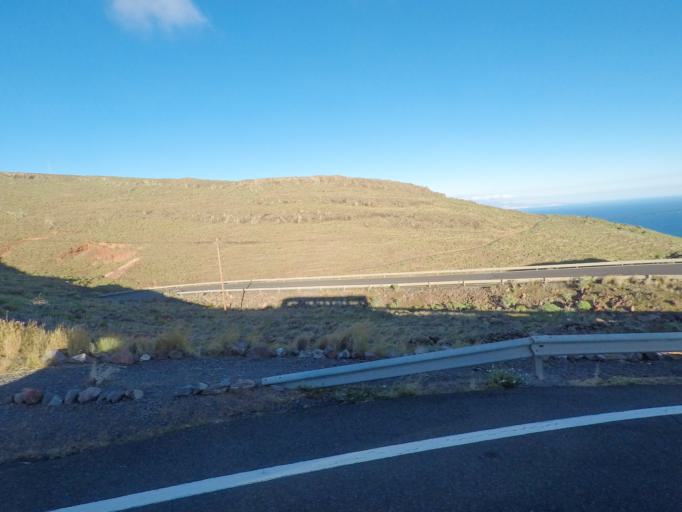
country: ES
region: Canary Islands
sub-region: Provincia de Santa Cruz de Tenerife
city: San Sebastian de la Gomera
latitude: 28.0919
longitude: -17.1520
